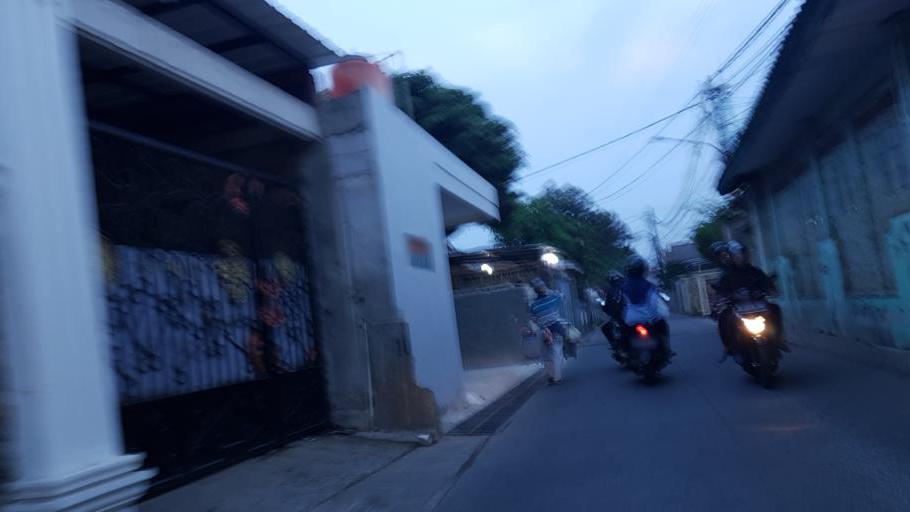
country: ID
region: West Java
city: Pamulang
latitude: -6.3240
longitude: 106.7939
